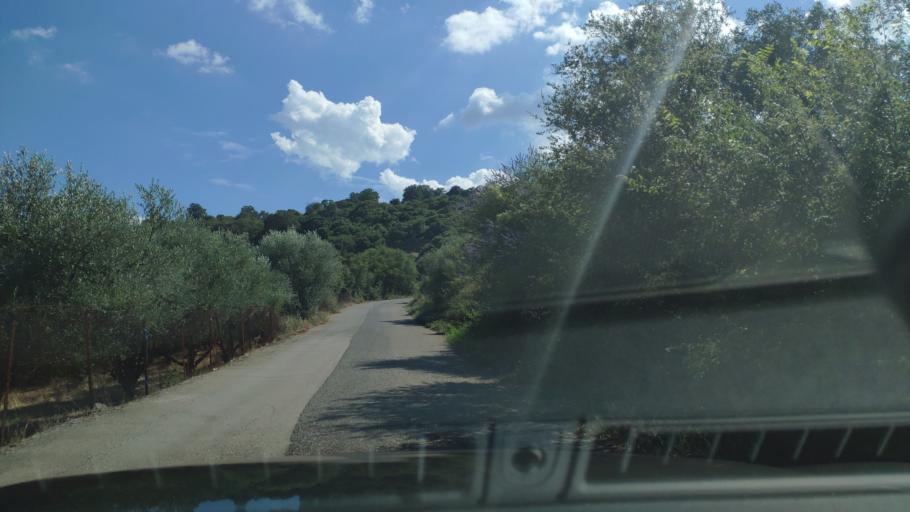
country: GR
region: West Greece
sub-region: Nomos Aitolias kai Akarnanias
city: Katouna
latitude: 38.8130
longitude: 21.1060
